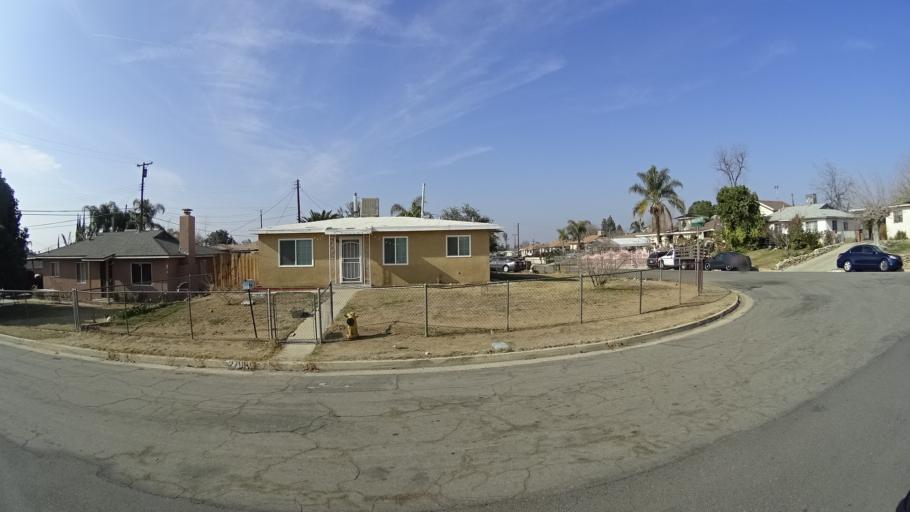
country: US
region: California
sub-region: Kern County
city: Bakersfield
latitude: 35.3922
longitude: -118.9696
